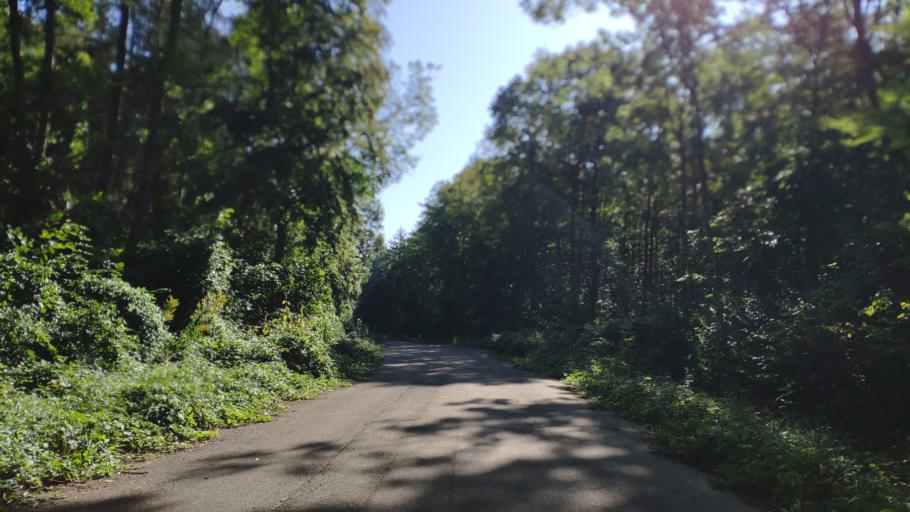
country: DE
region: Baden-Wuerttemberg
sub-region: Tuebingen Region
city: Ulm
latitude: 48.4177
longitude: 9.9590
